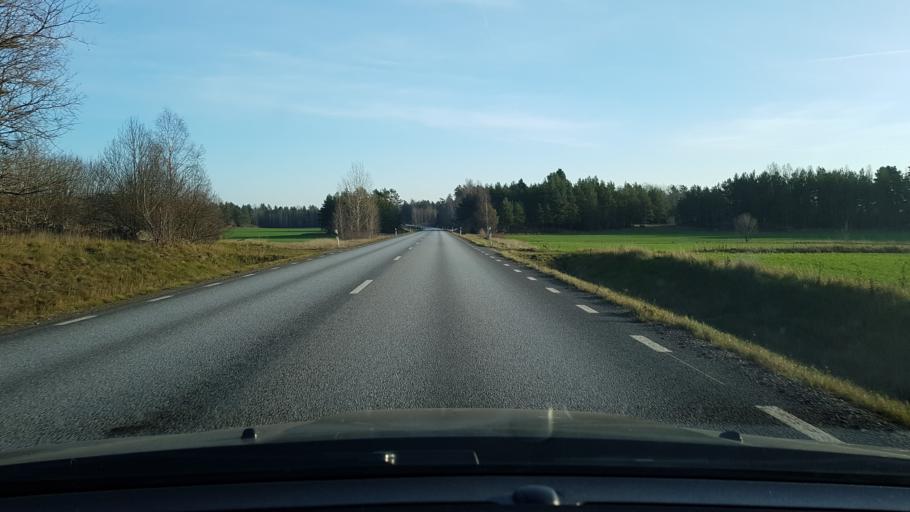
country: SE
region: Stockholm
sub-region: Vallentuna Kommun
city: Vallentuna
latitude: 59.7482
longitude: 18.0720
